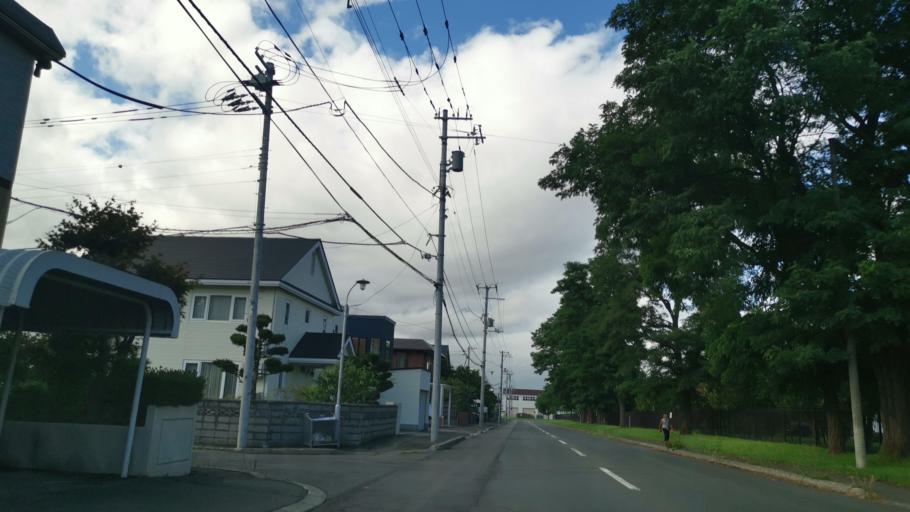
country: JP
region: Hokkaido
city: Sapporo
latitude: 42.9987
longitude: 141.3559
